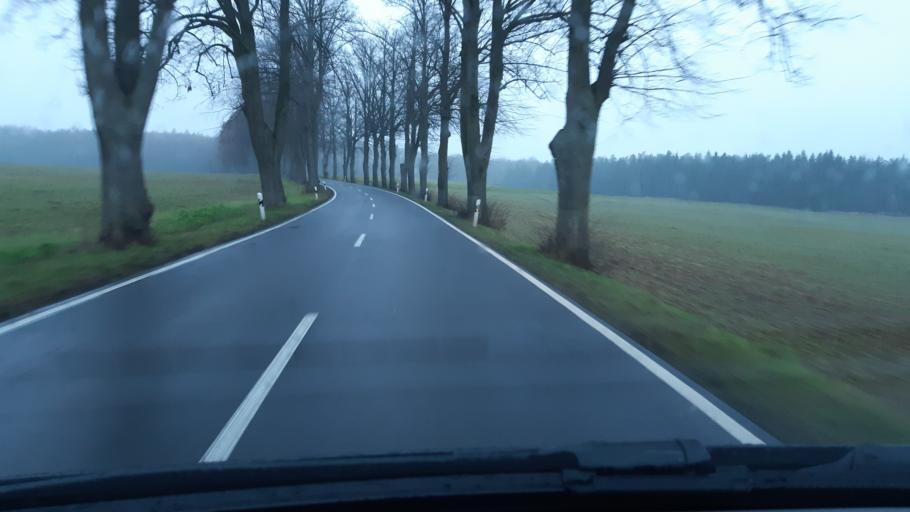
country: DE
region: Brandenburg
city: Mittenwalde
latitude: 53.1700
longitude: 13.6540
